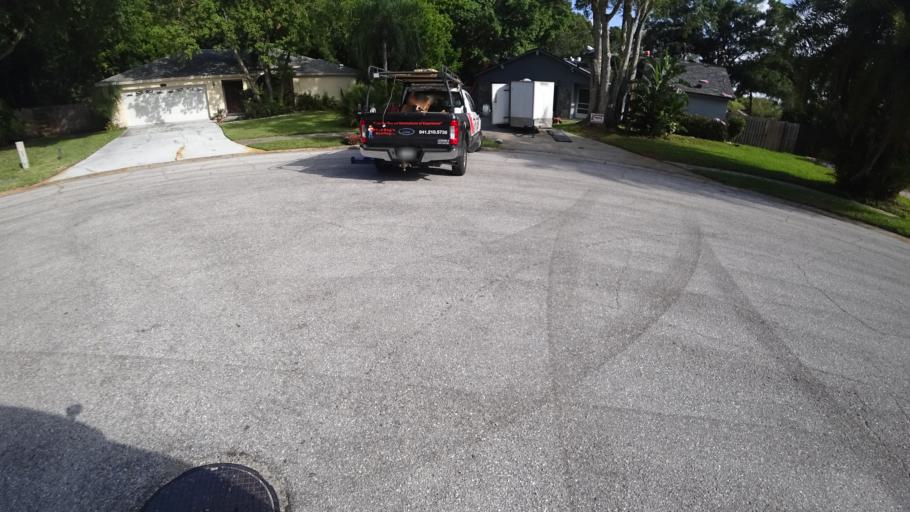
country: US
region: Florida
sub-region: Sarasota County
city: Desoto Lakes
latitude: 27.3917
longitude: -82.5010
